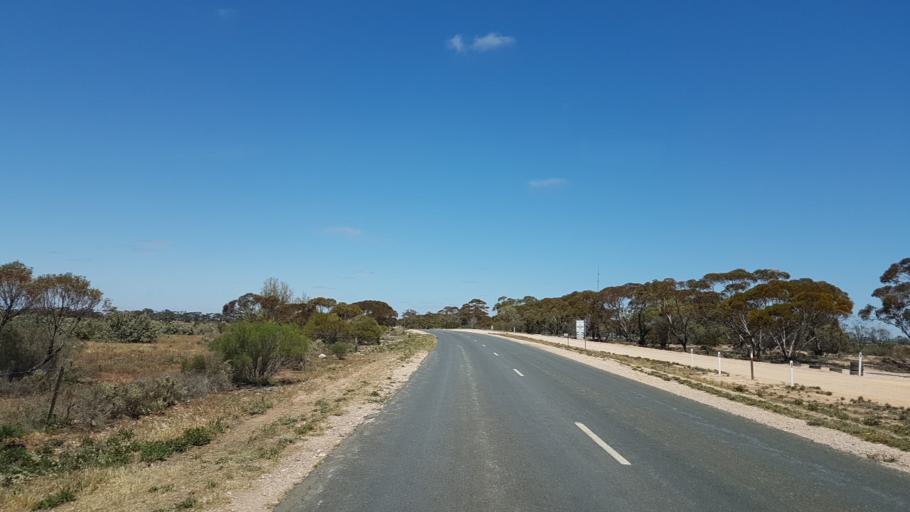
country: AU
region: South Australia
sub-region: Loxton Waikerie
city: Waikerie
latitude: -34.1830
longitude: 140.0224
